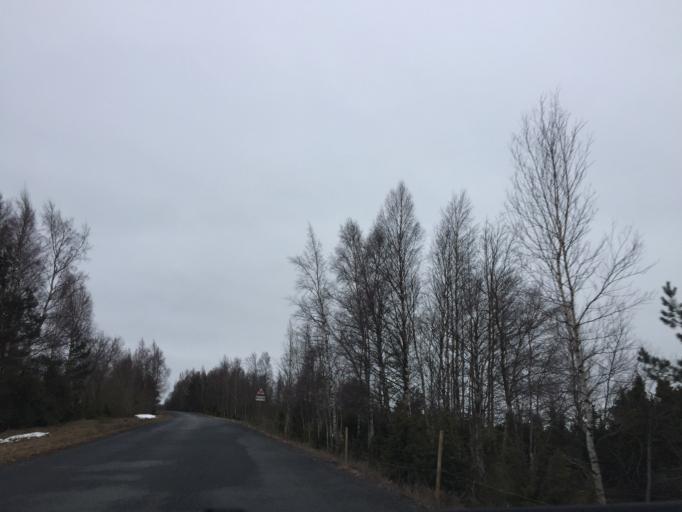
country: EE
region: Laeaene
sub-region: Haapsalu linn
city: Haapsalu
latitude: 58.7770
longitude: 23.4620
